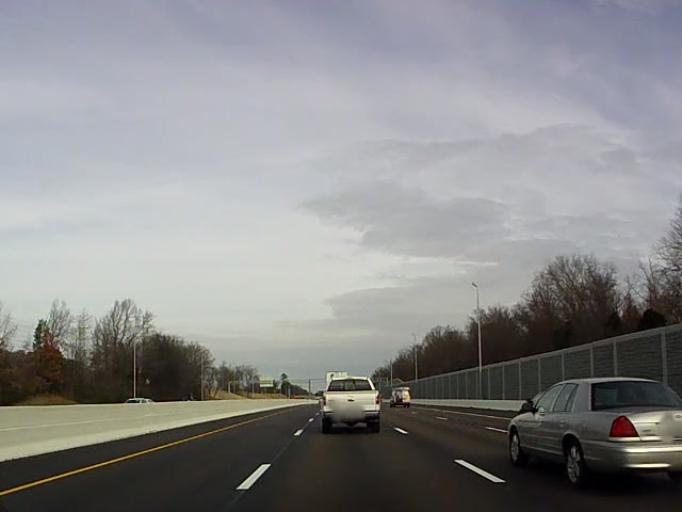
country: US
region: Tennessee
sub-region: Shelby County
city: Germantown
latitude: 35.1189
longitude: -89.8690
